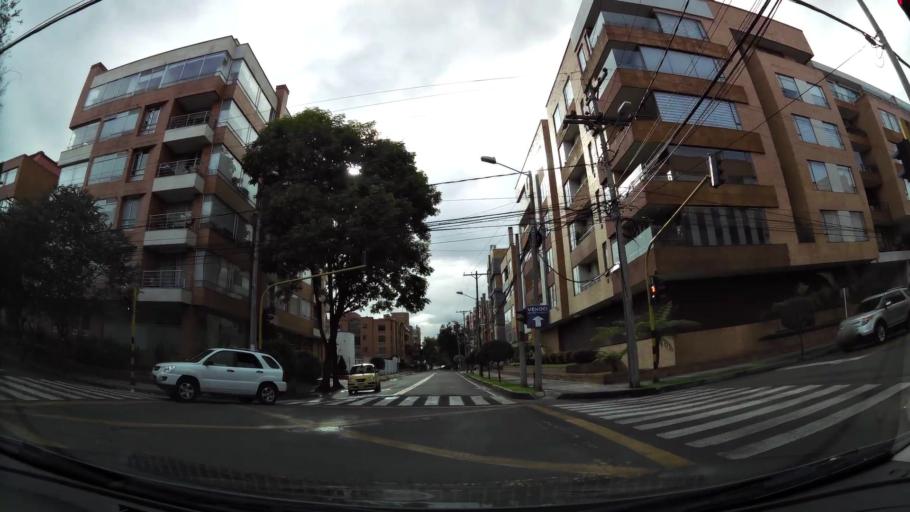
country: CO
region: Bogota D.C.
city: Barrio San Luis
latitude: 4.6888
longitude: -74.0532
